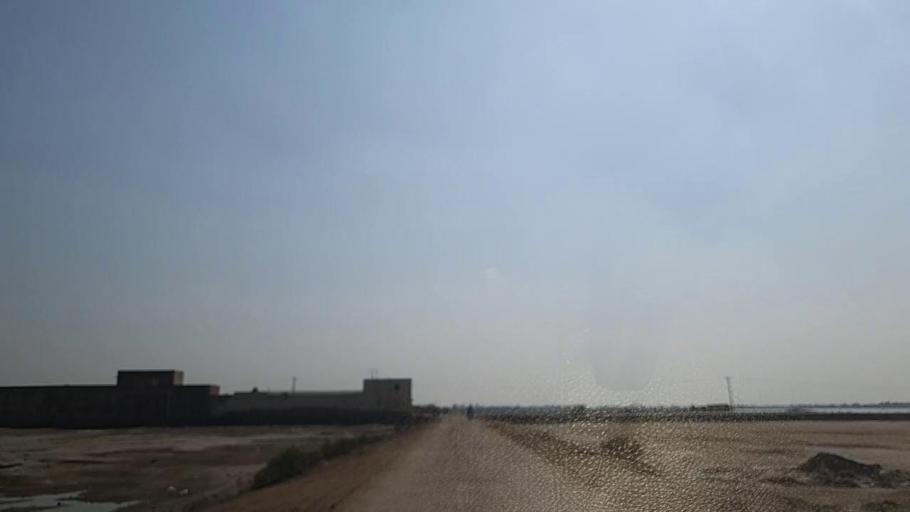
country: PK
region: Sindh
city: Daur
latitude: 26.4638
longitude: 68.2504
